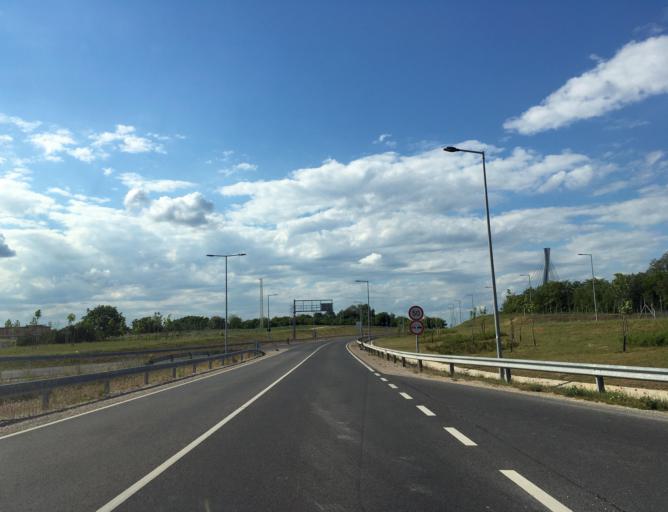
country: HU
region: Komarom-Esztergom
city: Komarom
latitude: 47.7506
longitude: 18.0863
